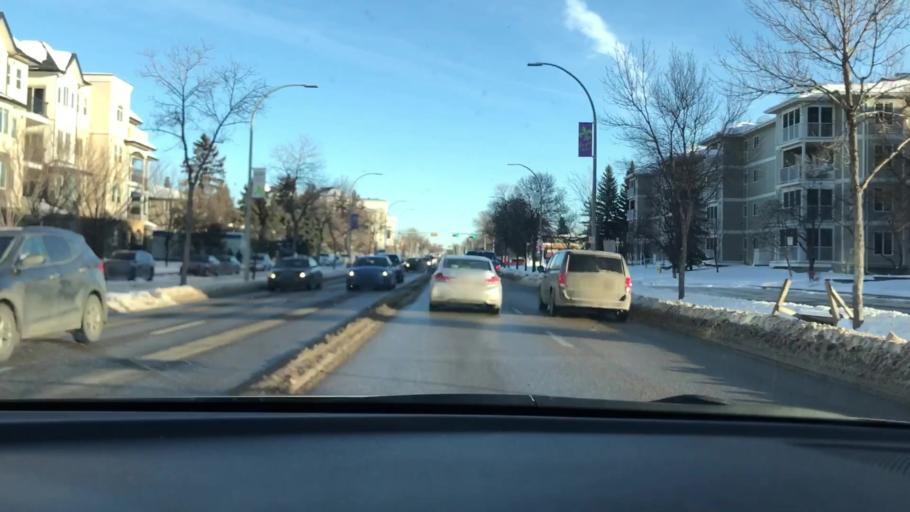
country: CA
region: Alberta
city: Edmonton
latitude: 53.5180
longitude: -113.4638
